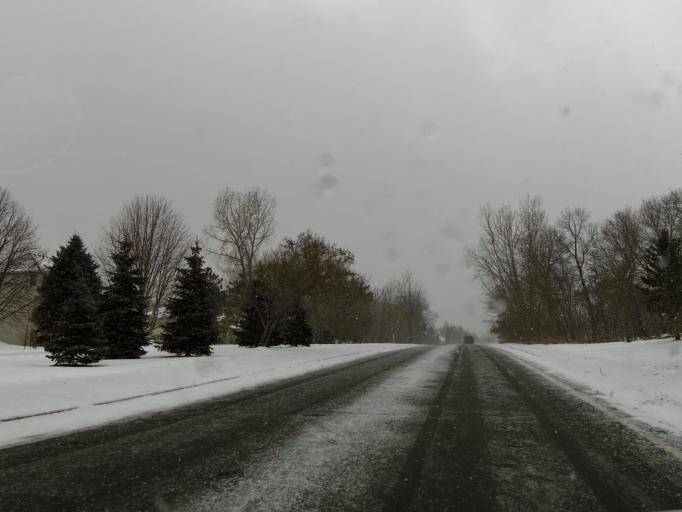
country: US
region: Minnesota
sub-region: Washington County
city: Woodbury
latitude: 44.9317
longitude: -92.9199
